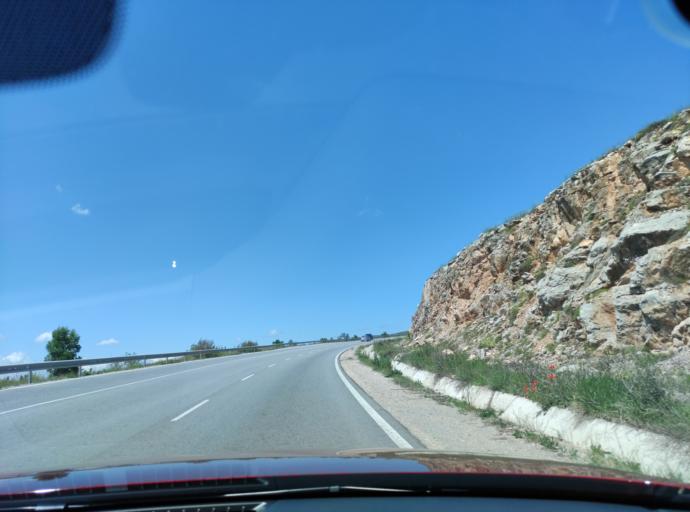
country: BG
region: Sofiya
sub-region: Obshtina Kostinbrod
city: Kostinbrod
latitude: 42.8911
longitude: 23.1556
